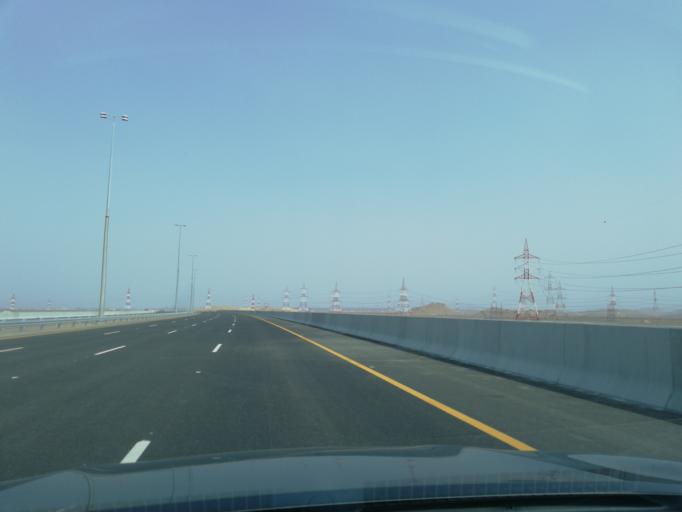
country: OM
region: Al Batinah
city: Al Sohar
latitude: 24.3324
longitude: 56.5574
